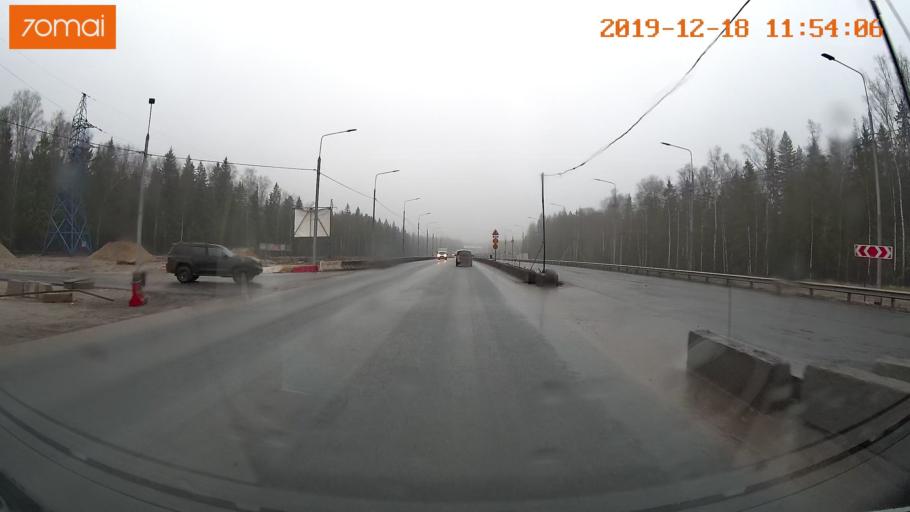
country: RU
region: Moskovskaya
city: Yershovo
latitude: 55.8121
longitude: 36.9187
